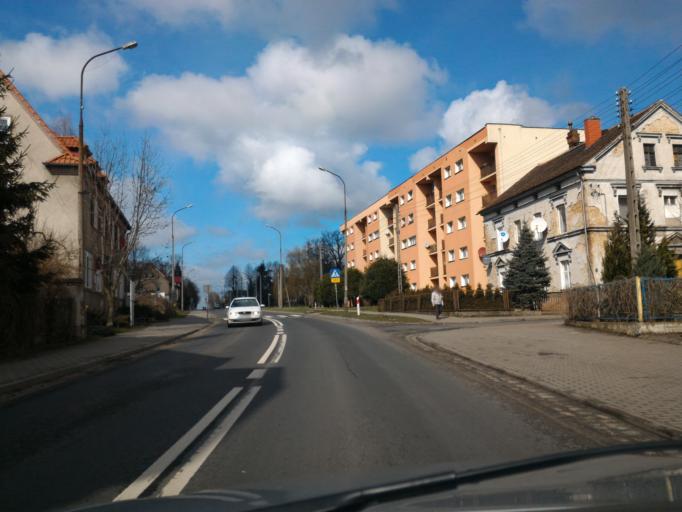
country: PL
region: Silesian Voivodeship
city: Zawidow
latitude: 51.0267
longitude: 15.0615
